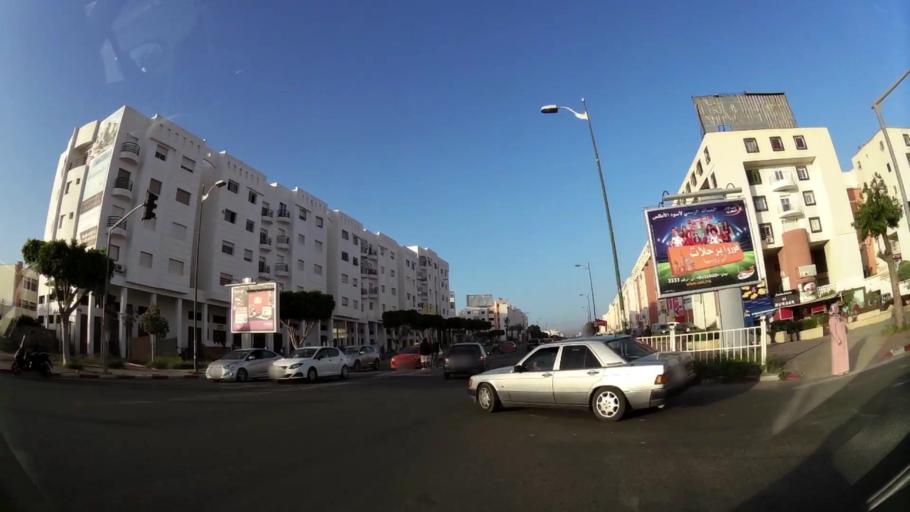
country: MA
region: Oued ed Dahab-Lagouira
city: Dakhla
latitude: 30.4170
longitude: -9.5657
